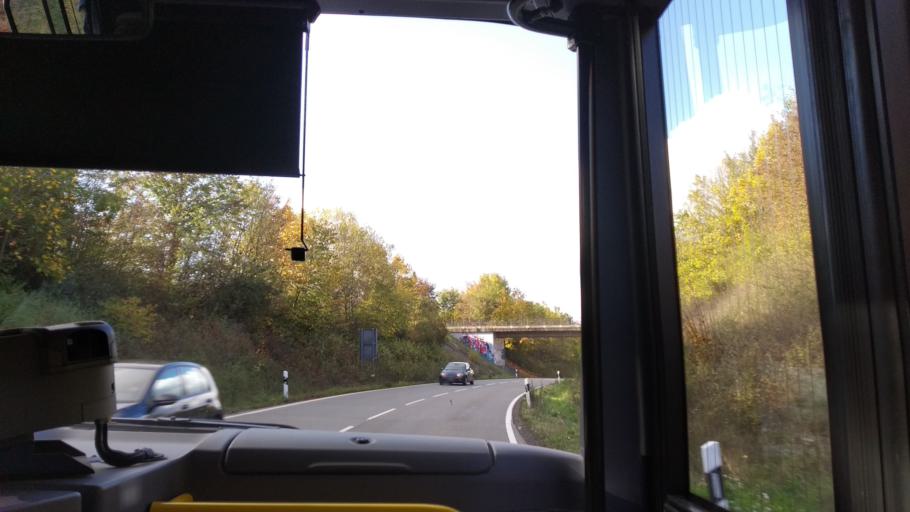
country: DE
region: Rheinland-Pfalz
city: Diez
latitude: 50.3608
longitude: 8.0168
